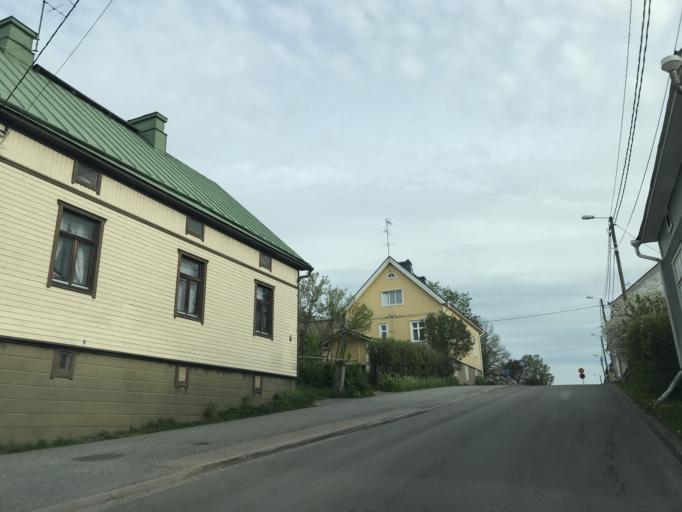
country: FI
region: Varsinais-Suomi
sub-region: Turku
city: Turku
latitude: 60.4541
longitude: 22.3076
